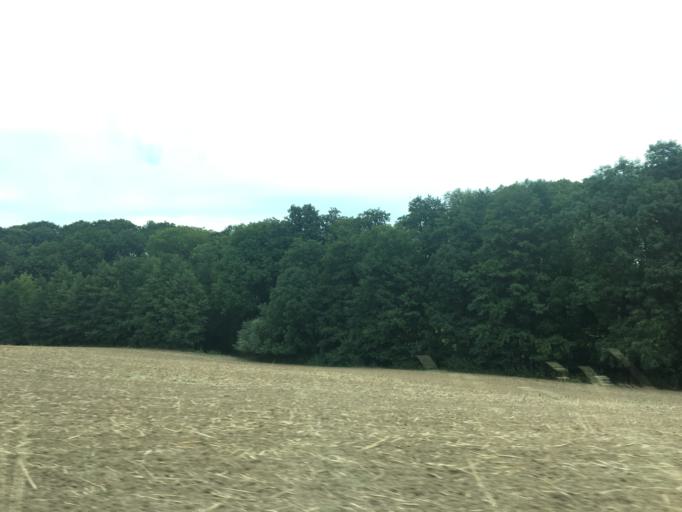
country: DE
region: Saxony
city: Wilsdruff
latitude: 51.0688
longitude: 13.5871
